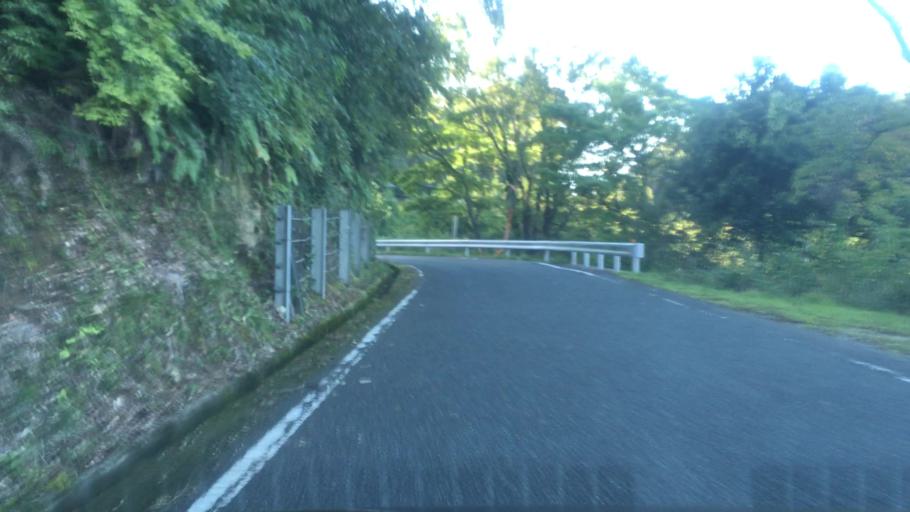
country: JP
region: Hyogo
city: Toyooka
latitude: 35.6174
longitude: 134.8747
